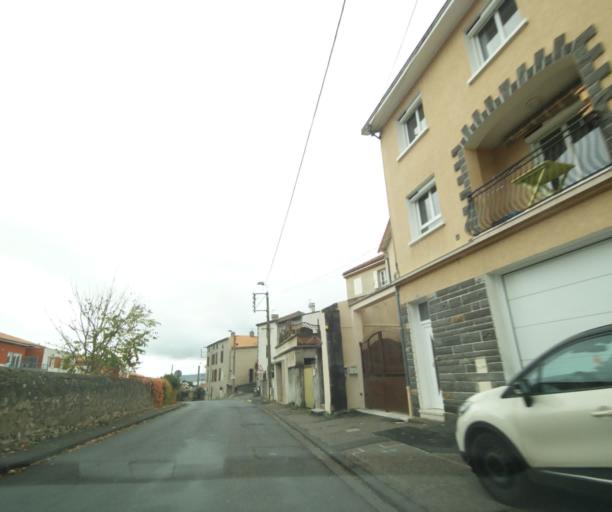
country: FR
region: Auvergne
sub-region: Departement du Puy-de-Dome
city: Cournon-d'Auvergne
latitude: 45.7415
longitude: 3.2002
